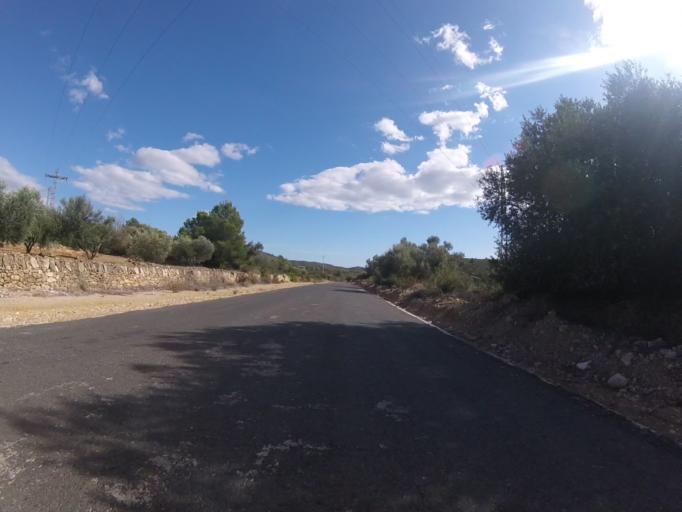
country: ES
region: Valencia
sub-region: Provincia de Castello
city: Alcala de Xivert
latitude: 40.2751
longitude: 0.2306
